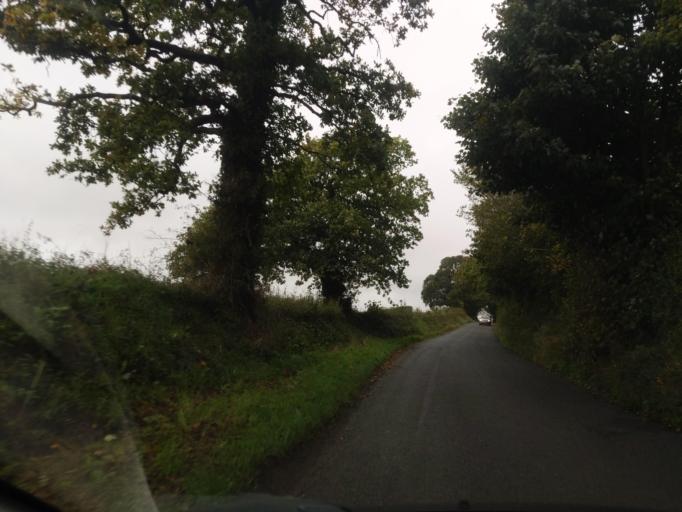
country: GB
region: England
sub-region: Cornwall
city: Saltash
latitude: 50.4439
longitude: -4.2220
